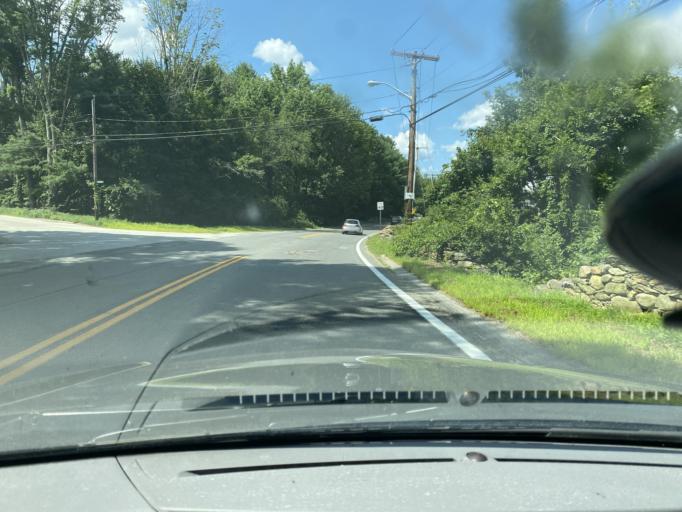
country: US
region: Rhode Island
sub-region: Providence County
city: North Scituate
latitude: 41.8427
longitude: -71.5854
